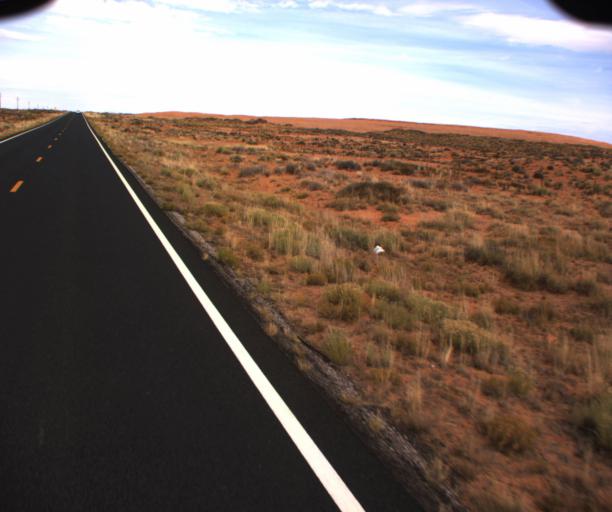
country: US
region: Arizona
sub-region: Apache County
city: Many Farms
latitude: 36.8203
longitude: -109.6454
